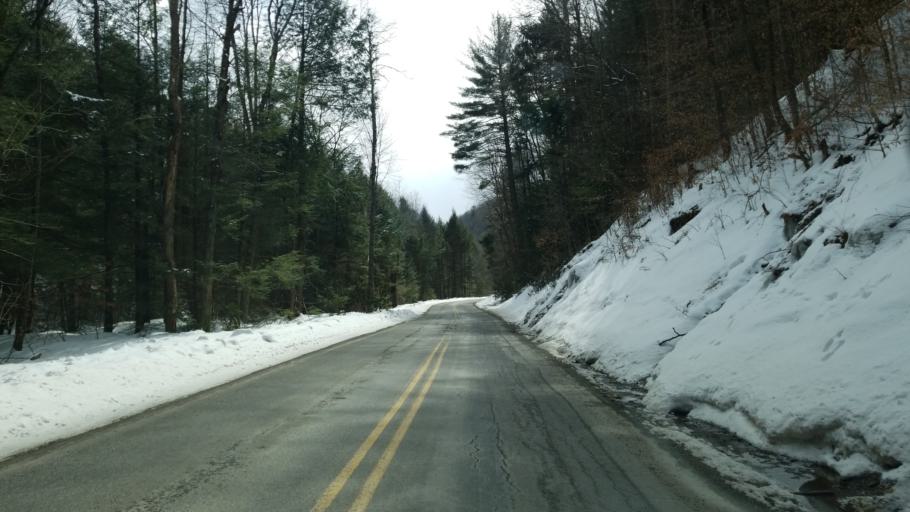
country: US
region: Pennsylvania
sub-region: Clearfield County
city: Shiloh
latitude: 41.2525
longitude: -78.1521
